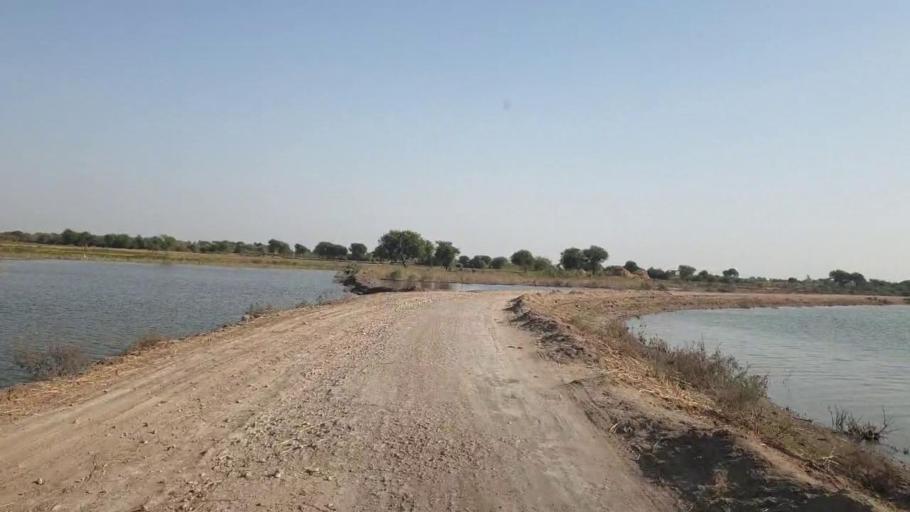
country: PK
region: Sindh
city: Matli
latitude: 25.0066
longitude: 68.7435
